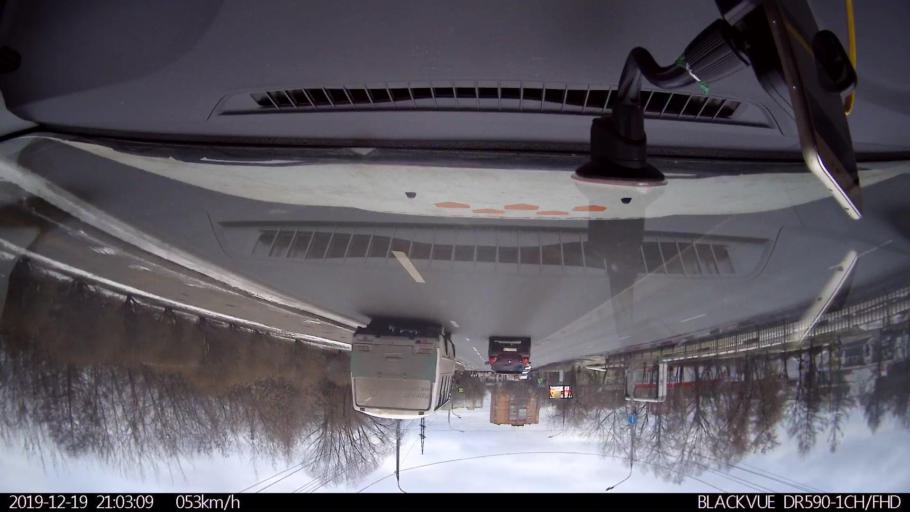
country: RU
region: Nizjnij Novgorod
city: Gorbatovka
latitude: 56.3463
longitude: 43.8440
